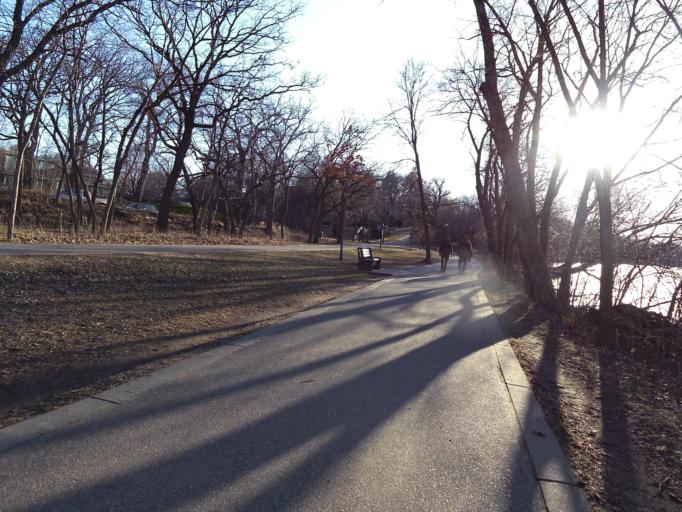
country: US
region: Minnesota
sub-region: Hennepin County
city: Richfield
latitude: 44.9159
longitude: -93.3032
